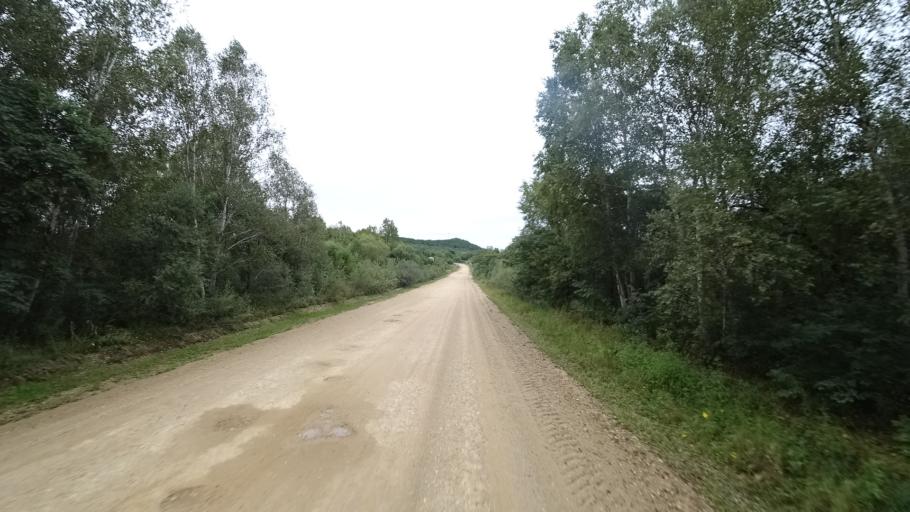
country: RU
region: Primorskiy
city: Rettikhovka
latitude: 44.1650
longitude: 132.7335
